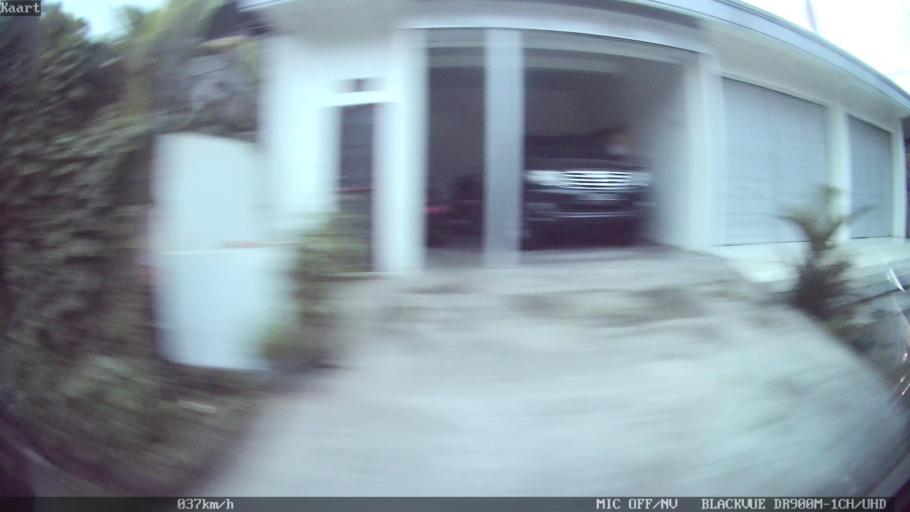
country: ID
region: Bali
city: Banjar Tengah
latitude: -8.4491
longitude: 115.2782
